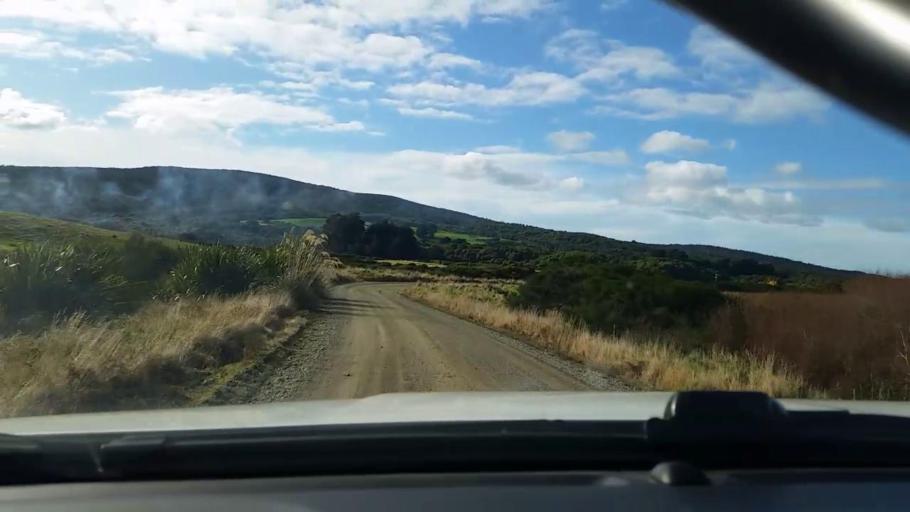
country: NZ
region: Southland
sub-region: Southland District
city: Riverton
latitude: -46.3332
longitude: 167.8181
